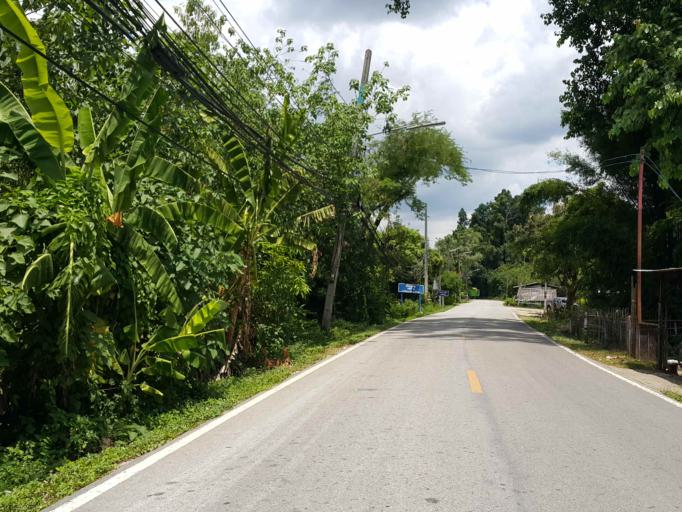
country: TH
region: Chiang Mai
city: Chiang Mai
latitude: 18.7425
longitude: 98.9946
